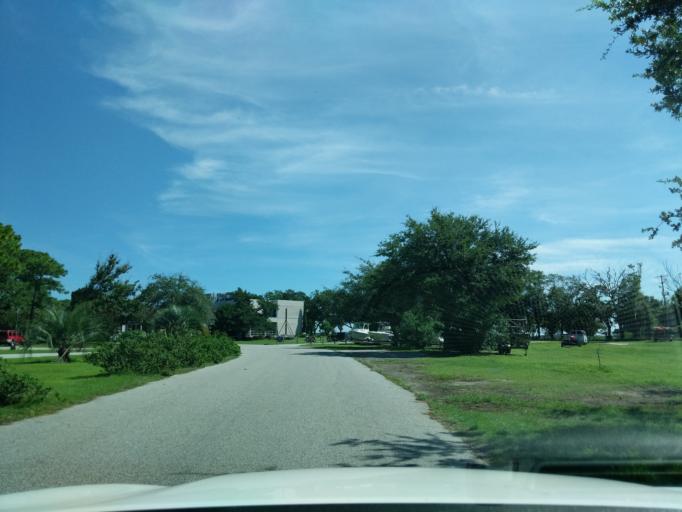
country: US
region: South Carolina
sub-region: Charleston County
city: Charleston
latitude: 32.7508
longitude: -79.8989
